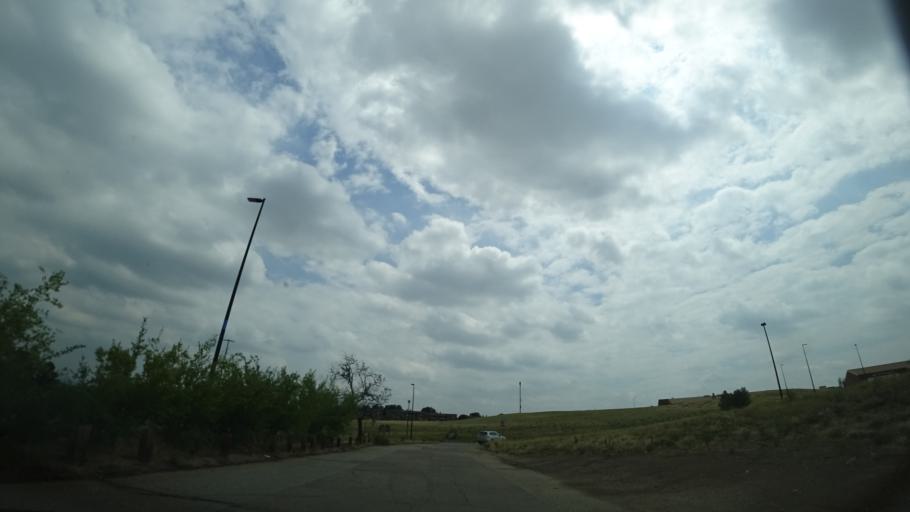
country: US
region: Colorado
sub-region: Jefferson County
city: West Pleasant View
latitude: 39.7172
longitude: -105.1506
